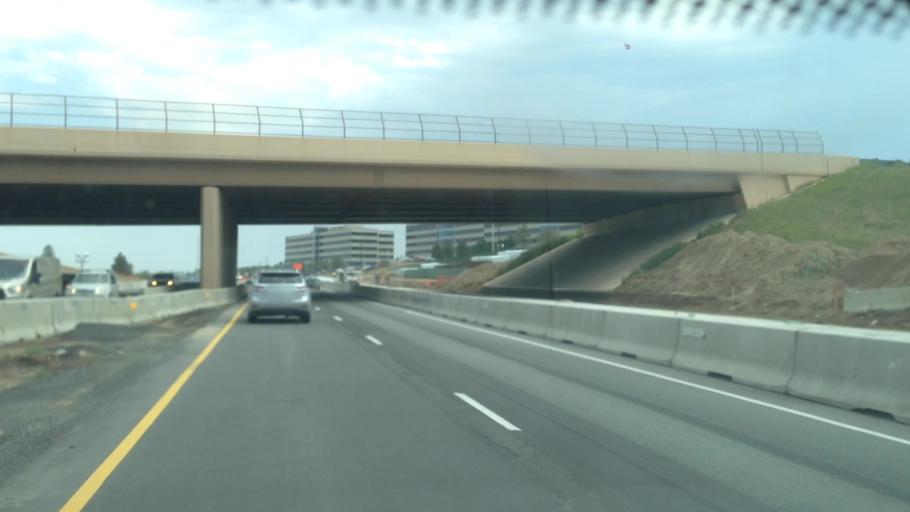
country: US
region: Colorado
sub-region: Douglas County
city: Highlands Ranch
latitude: 39.5601
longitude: -105.0088
